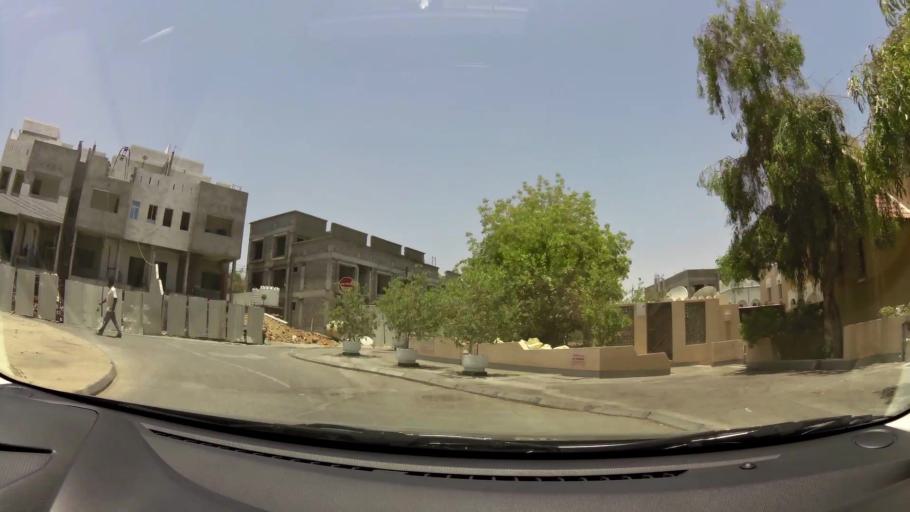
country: OM
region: Muhafazat Masqat
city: Bawshar
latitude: 23.6029
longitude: 58.4517
